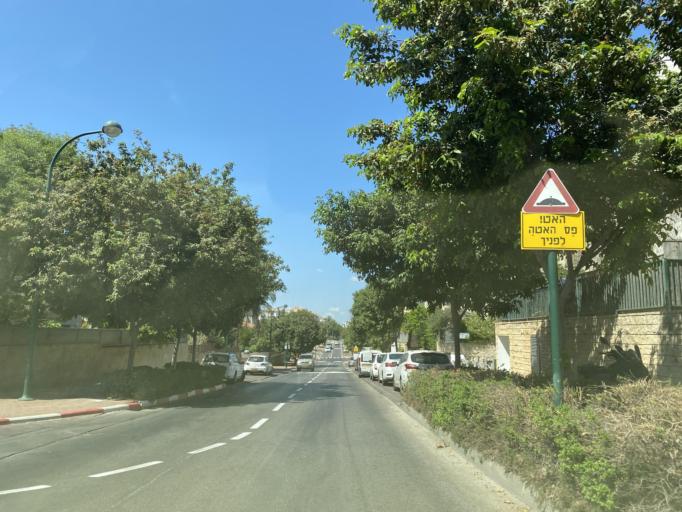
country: IL
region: Central District
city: Ra'anana
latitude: 32.1855
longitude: 34.8865
